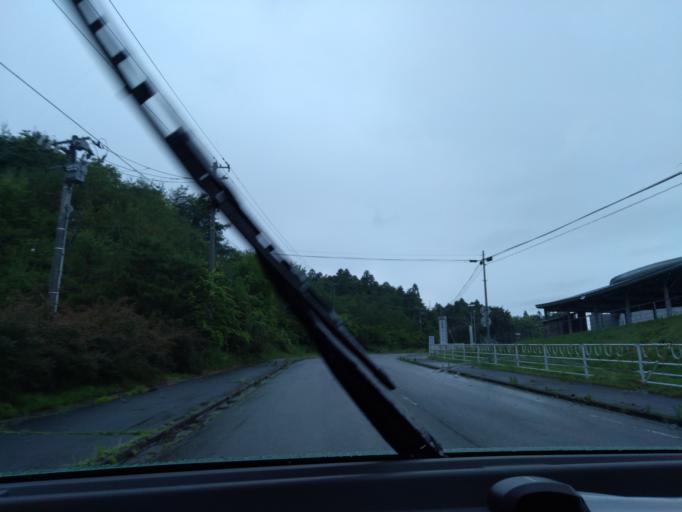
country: JP
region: Iwate
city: Ichinoseki
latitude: 38.8403
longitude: 141.0029
